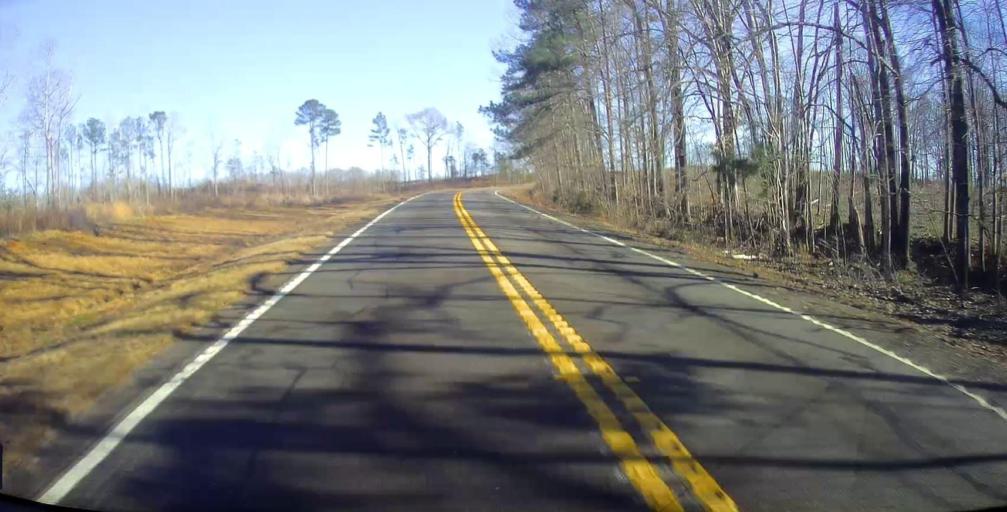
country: US
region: Georgia
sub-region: Talbot County
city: Talbotton
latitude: 32.6688
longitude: -84.4666
